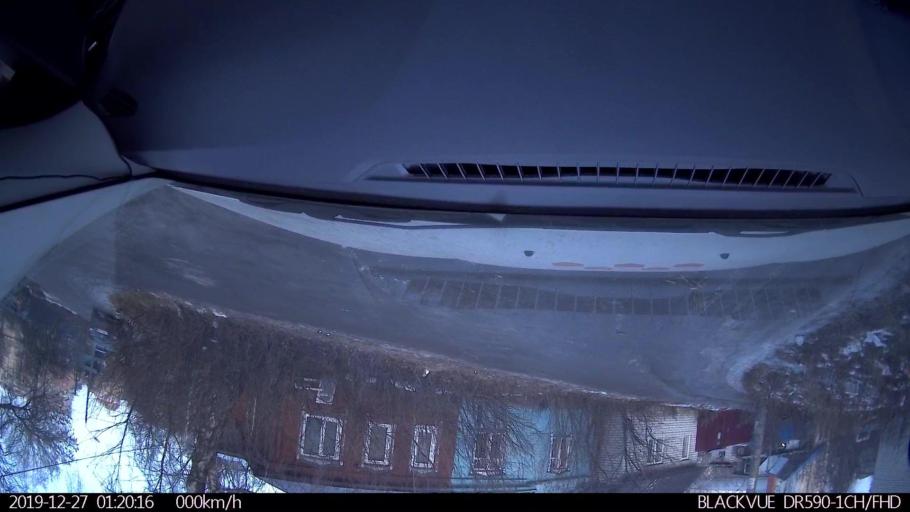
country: RU
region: Nizjnij Novgorod
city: Nizhniy Novgorod
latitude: 56.3040
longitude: 43.9910
